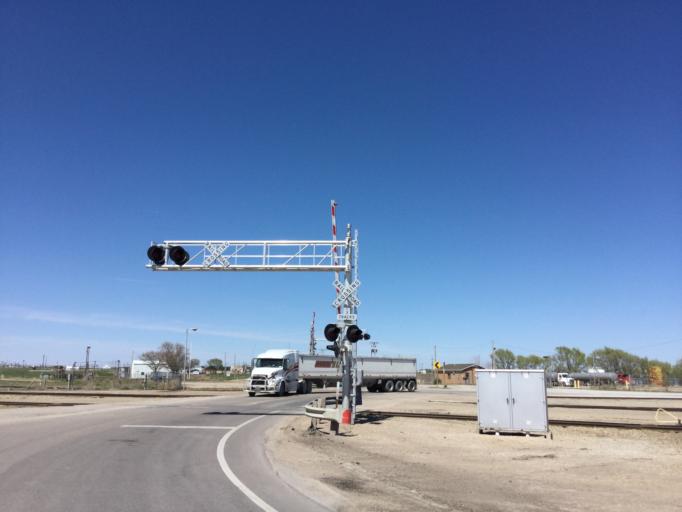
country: US
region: Kansas
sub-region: Phillips County
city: Phillipsburg
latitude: 39.7700
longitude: -99.3289
